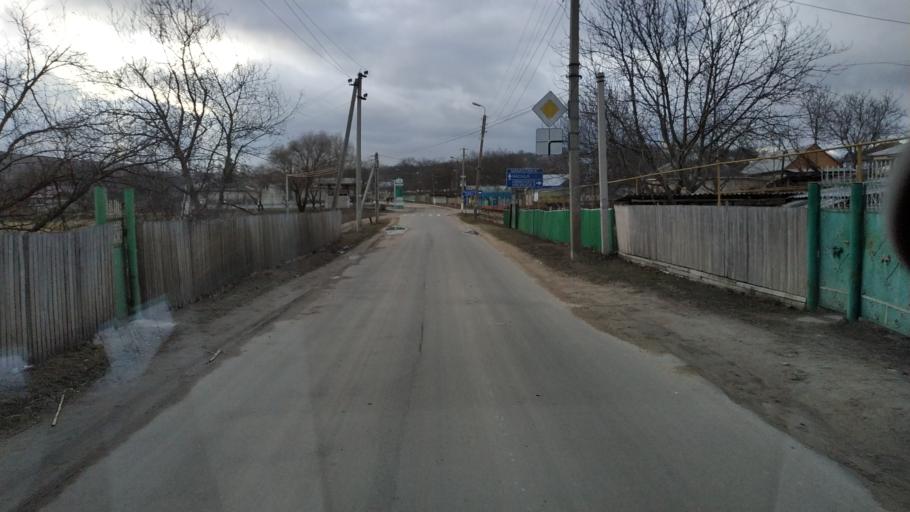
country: MD
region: Calarasi
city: Calarasi
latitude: 47.3067
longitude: 28.3620
